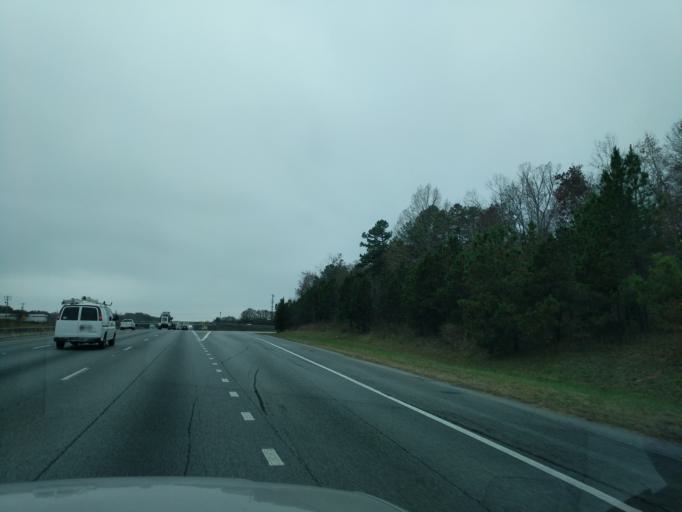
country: US
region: South Carolina
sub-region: Anderson County
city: Piedmont
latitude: 34.7169
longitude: -82.4975
